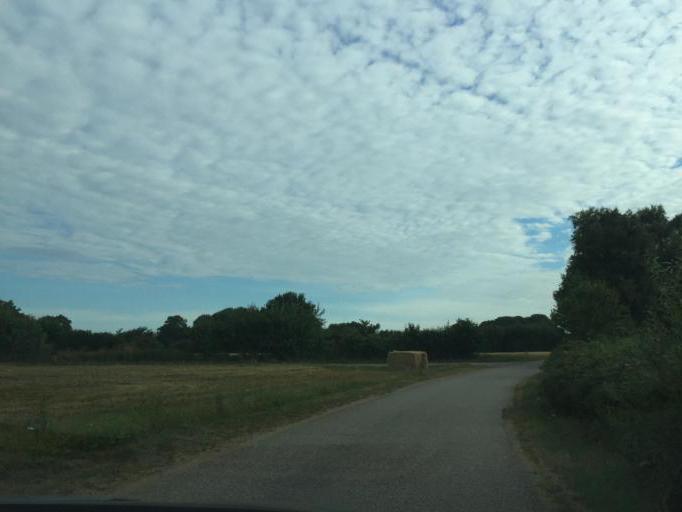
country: DK
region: South Denmark
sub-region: Assens Kommune
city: Assens
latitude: 55.2670
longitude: 9.9691
